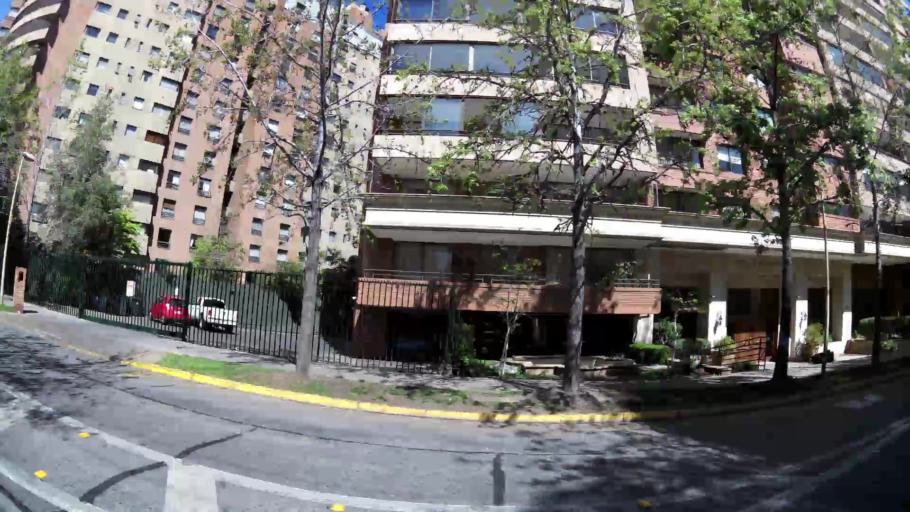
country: CL
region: Santiago Metropolitan
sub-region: Provincia de Santiago
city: Villa Presidente Frei, Nunoa, Santiago, Chile
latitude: -33.4212
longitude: -70.5745
